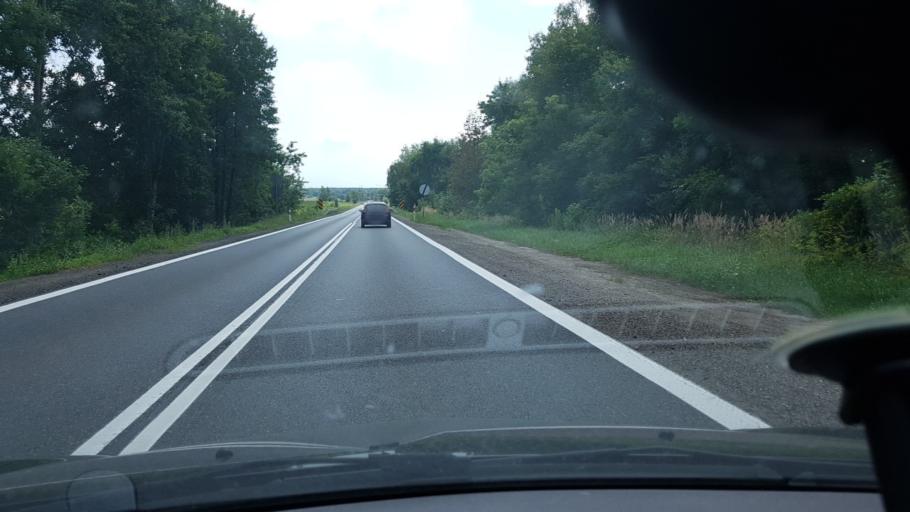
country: PL
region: Silesian Voivodeship
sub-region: Powiat bierunsko-ledzinski
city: Bierun
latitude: 50.0972
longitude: 19.1003
